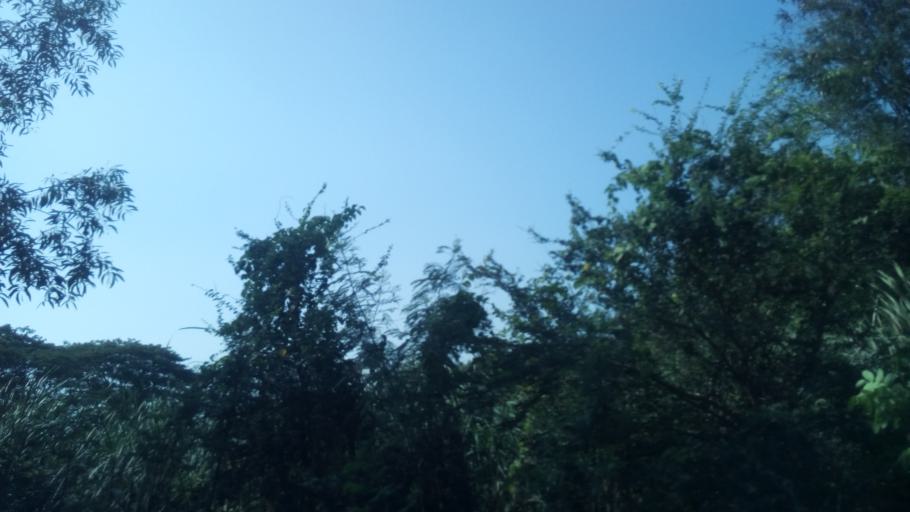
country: TH
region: Nonthaburi
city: Bang Yai
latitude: 13.8780
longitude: 100.2992
